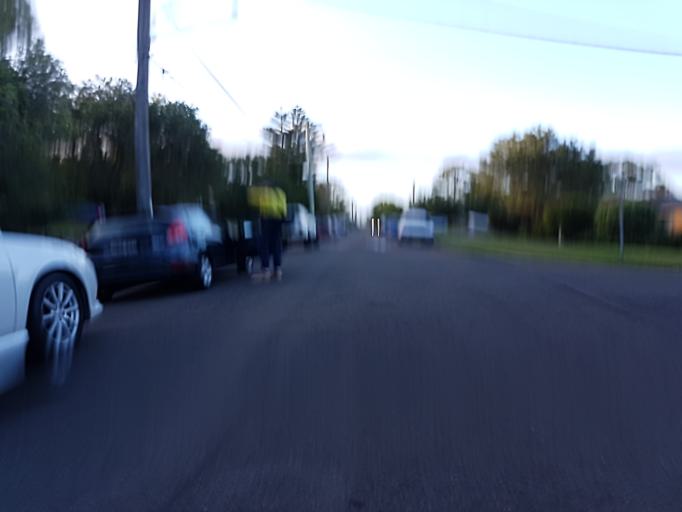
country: AU
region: New South Wales
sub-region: Warringah
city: Allambie Heights
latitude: -33.7531
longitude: 151.2305
